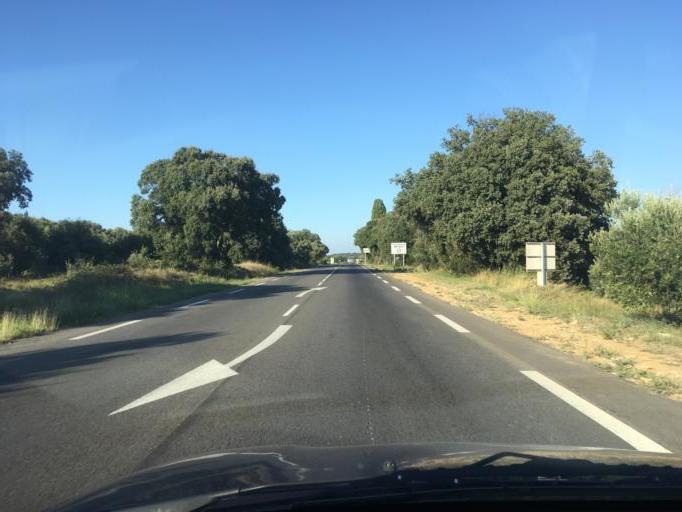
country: FR
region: Languedoc-Roussillon
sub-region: Departement du Gard
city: Bezouce
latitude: 43.8916
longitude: 4.5084
